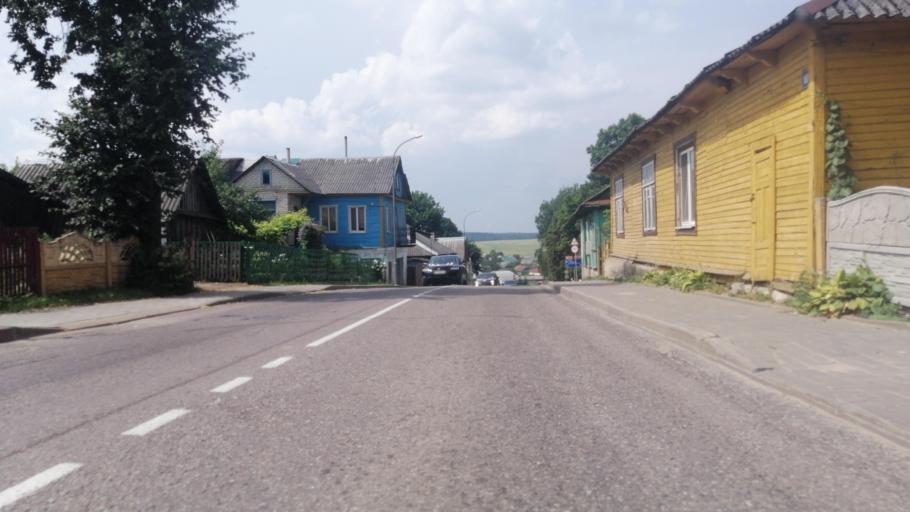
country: BY
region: Grodnenskaya
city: Navahrudak
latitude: 53.6004
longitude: 25.8250
